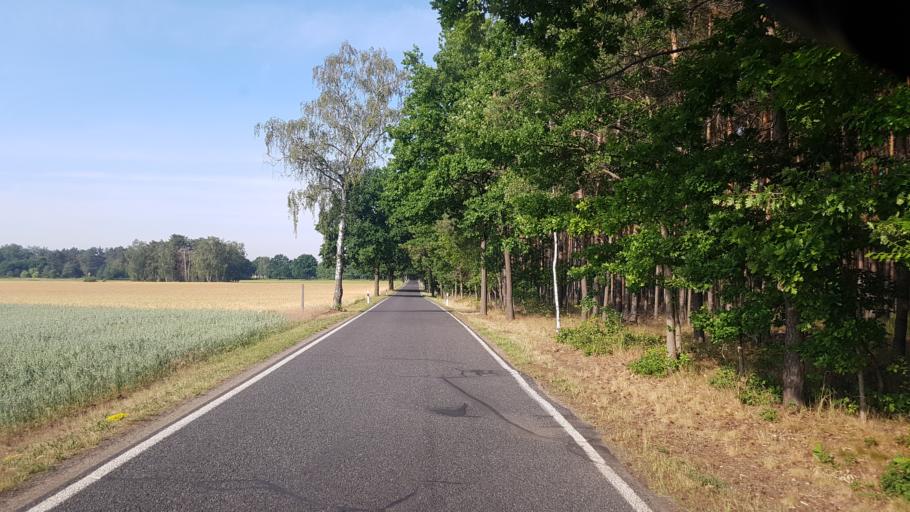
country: DE
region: Brandenburg
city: Ruckersdorf
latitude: 51.6078
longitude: 13.6291
